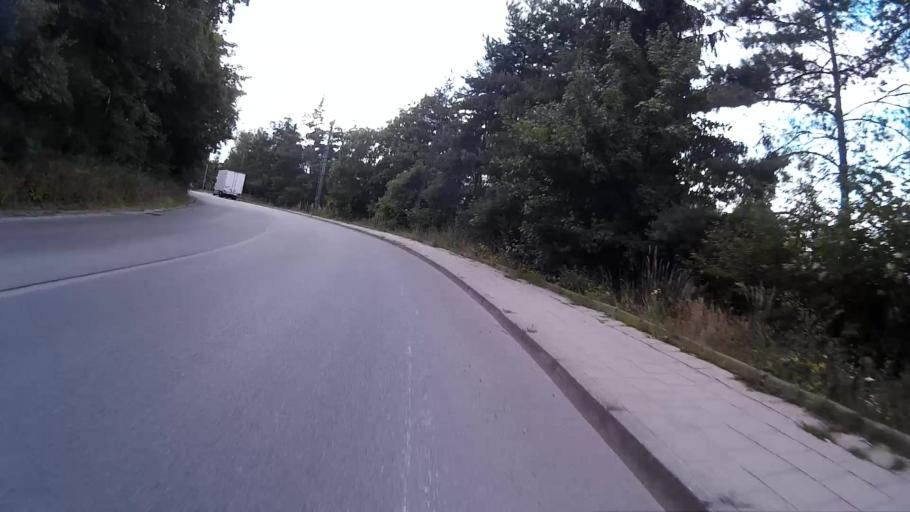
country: CZ
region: South Moravian
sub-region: Okres Brno-Venkov
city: Rosice
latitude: 49.1847
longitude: 16.3872
